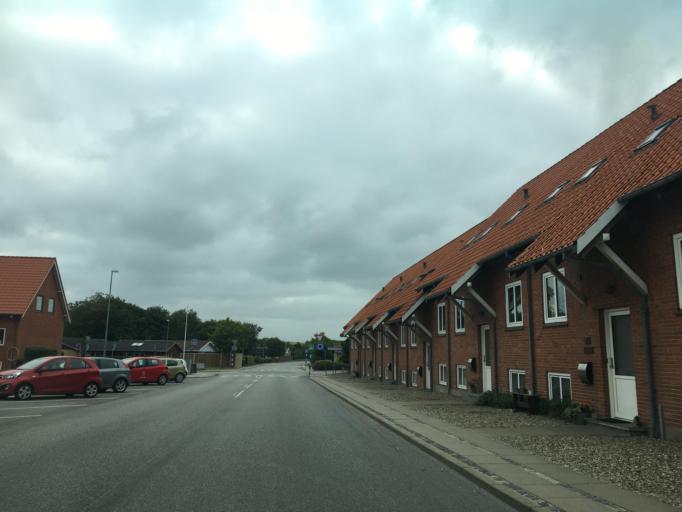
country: DK
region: North Denmark
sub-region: Thisted Kommune
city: Hurup
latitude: 56.7522
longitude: 8.4228
